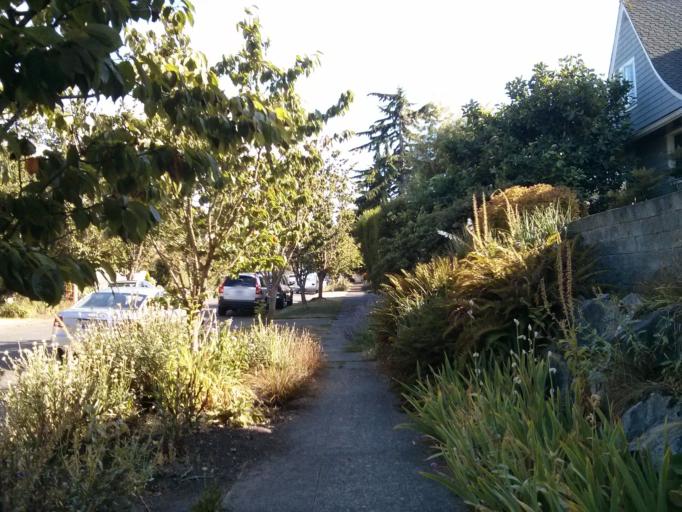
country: US
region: Washington
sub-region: King County
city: Seattle
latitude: 47.5868
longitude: -122.3919
